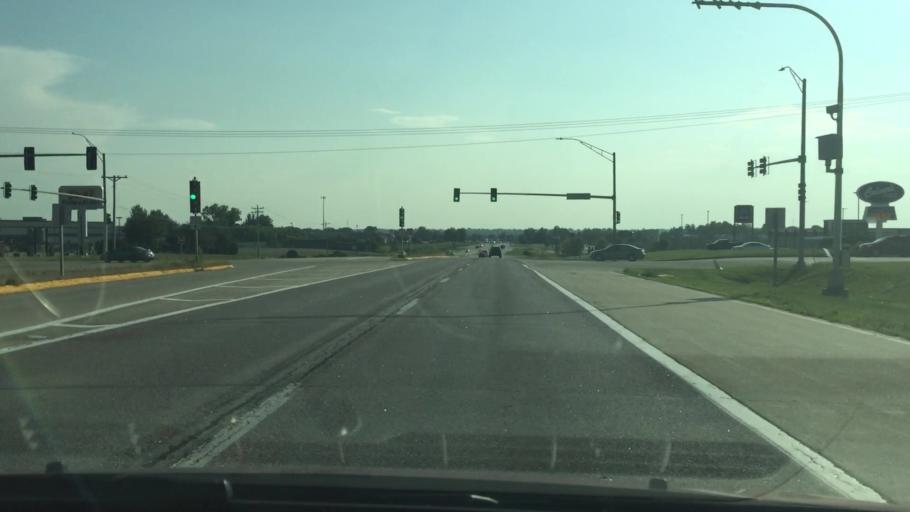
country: US
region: Iowa
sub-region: Muscatine County
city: Muscatine
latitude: 41.4598
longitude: -91.0170
